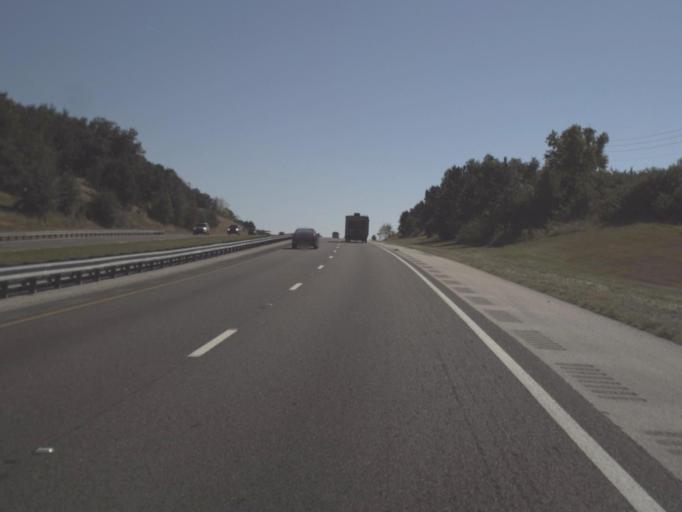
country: US
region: Florida
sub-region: Lake County
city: Montverde
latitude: 28.5738
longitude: -81.6982
